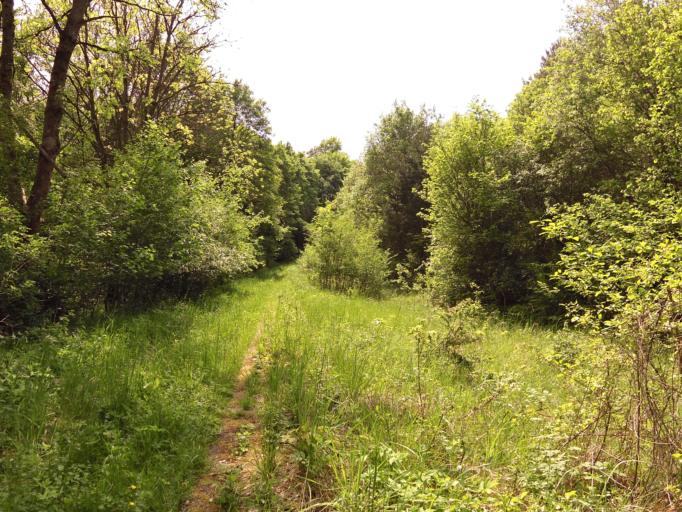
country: DE
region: Thuringia
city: Ifta
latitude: 51.0616
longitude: 10.1477
